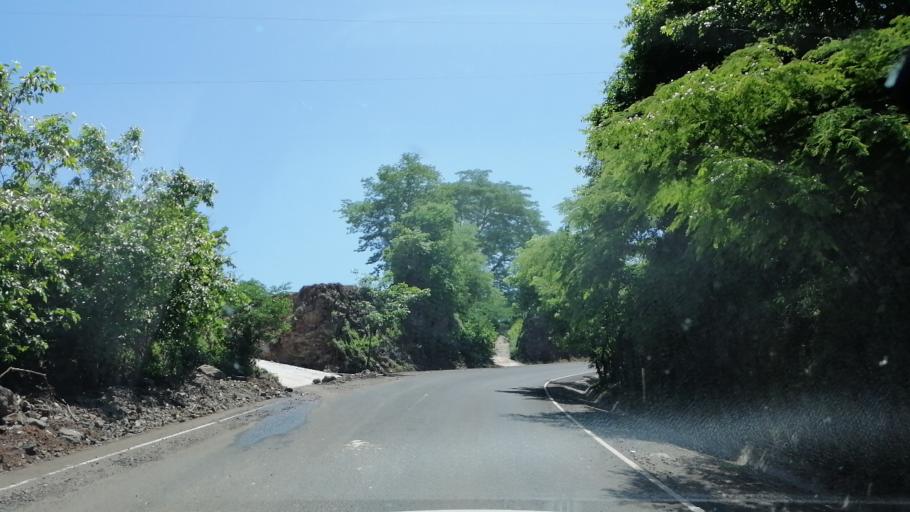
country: SV
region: San Miguel
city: Sesori
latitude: 13.8082
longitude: -88.4002
